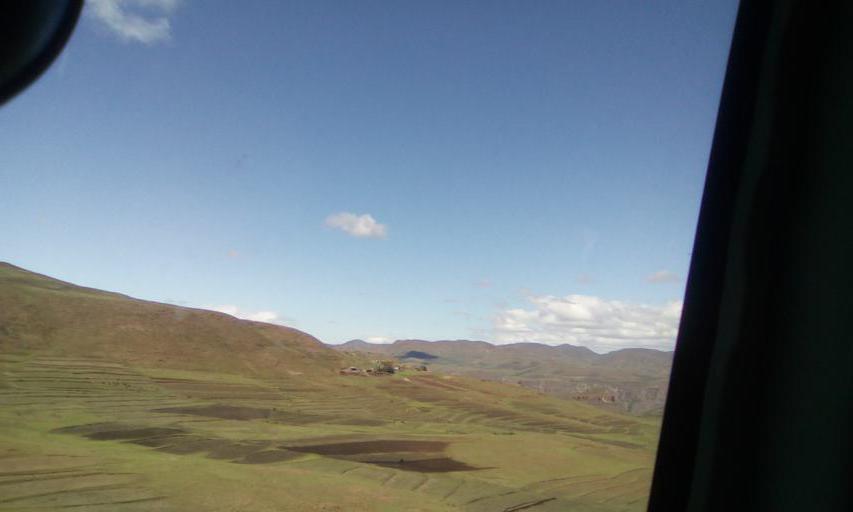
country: LS
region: Maseru
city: Nako
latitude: -29.8871
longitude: 28.1031
